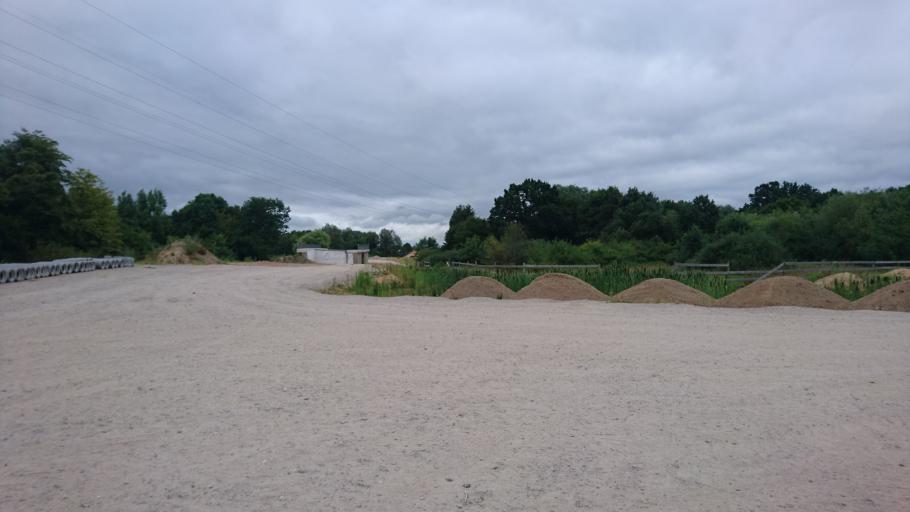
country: DE
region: Schleswig-Holstein
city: Pinneberg
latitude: 53.6646
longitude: 9.7758
